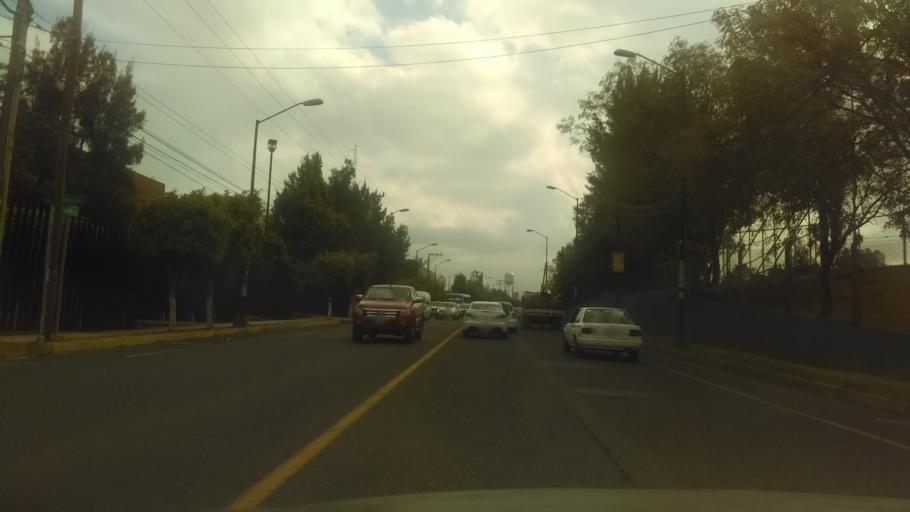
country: MX
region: Michoacan
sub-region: Morelia
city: Montana Monarca (Punta Altozano)
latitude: 19.6753
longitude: -101.1825
